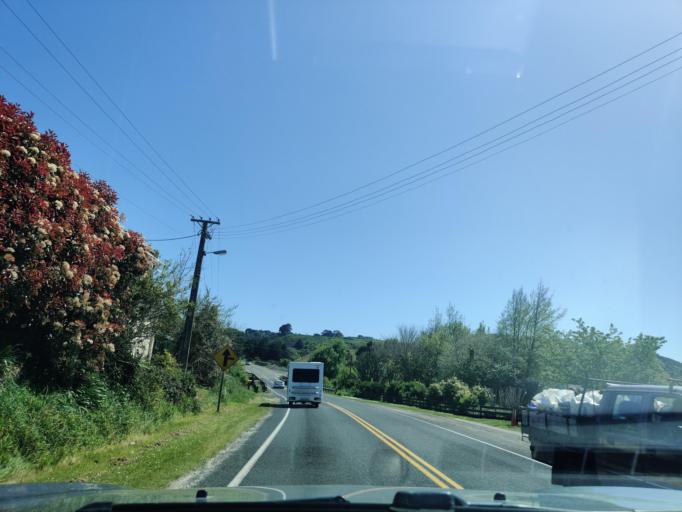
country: NZ
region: Manawatu-Wanganui
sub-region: Wanganui District
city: Wanganui
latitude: -39.8477
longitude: 174.9274
